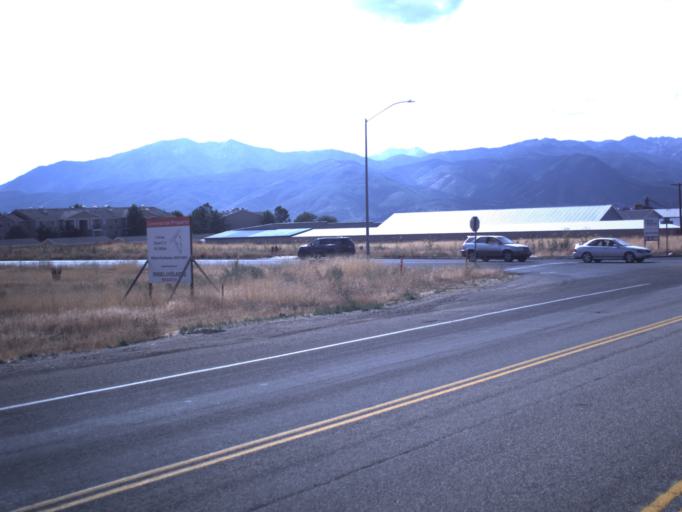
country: US
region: Utah
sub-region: Wasatch County
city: Heber
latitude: 40.4844
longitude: -111.4045
